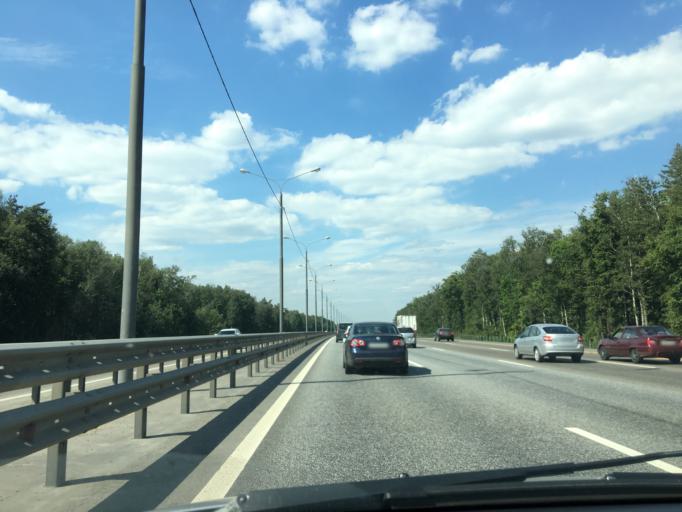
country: RU
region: Moskovskaya
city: Shcherbinka
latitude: 55.5129
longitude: 37.6087
